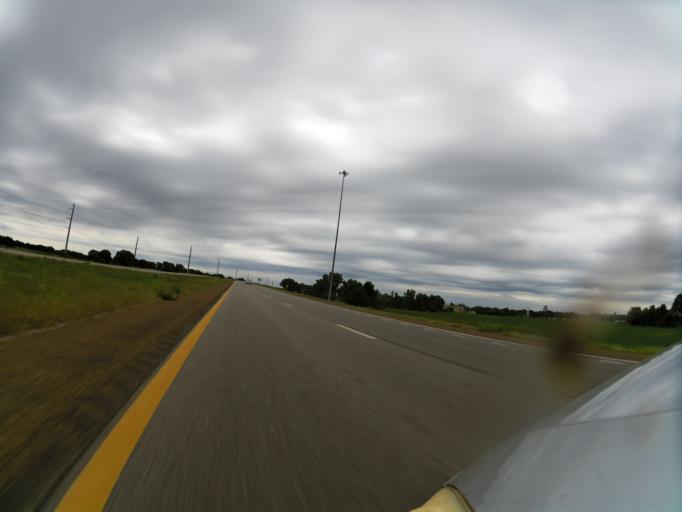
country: US
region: Kansas
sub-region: Sedgwick County
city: Maize
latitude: 37.7866
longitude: -97.4672
